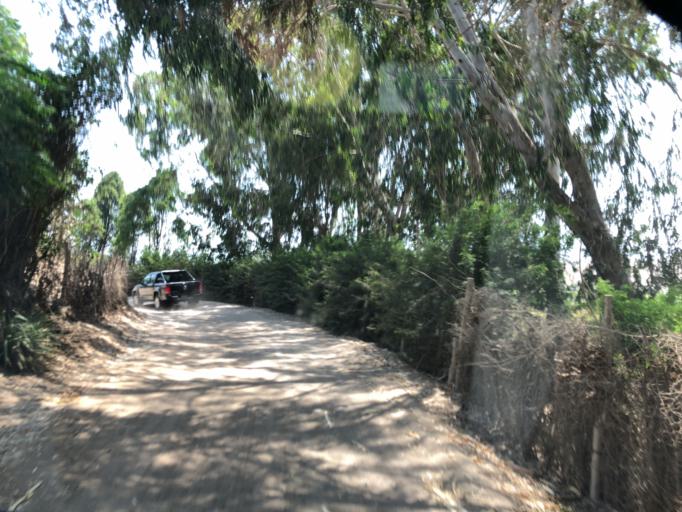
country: PE
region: Lima
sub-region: Provincia de Canete
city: Quilmana
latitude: -13.0083
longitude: -76.4585
